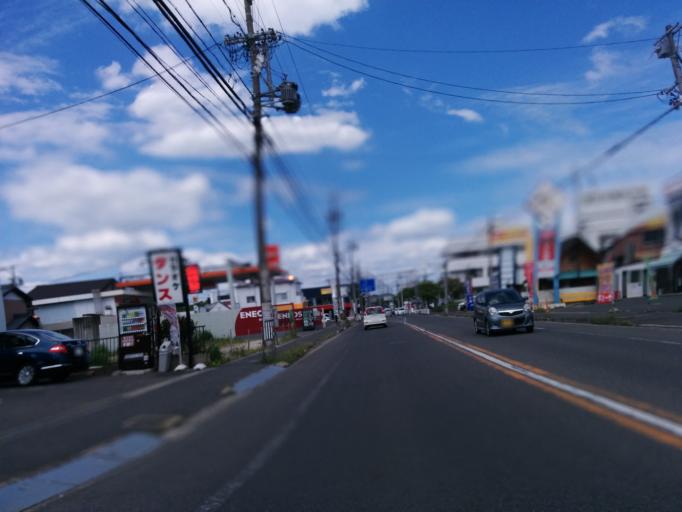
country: JP
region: Aichi
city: Kasugai
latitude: 35.2683
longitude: 136.9842
